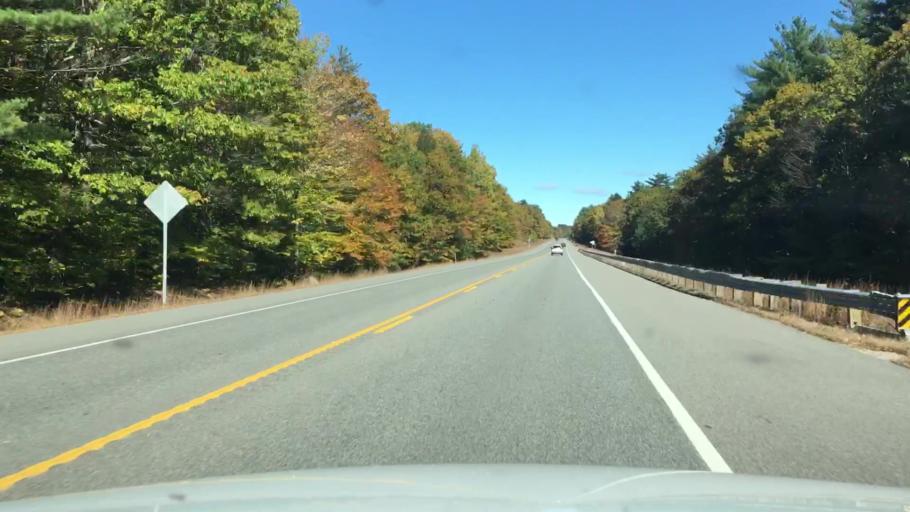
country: US
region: New Hampshire
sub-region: Carroll County
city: Sanbornville
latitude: 43.5043
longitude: -71.0293
